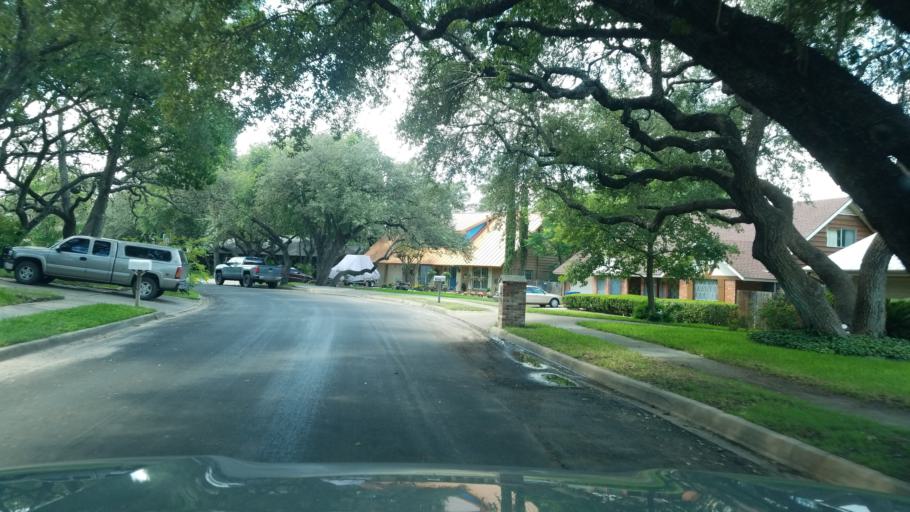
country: US
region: Texas
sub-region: Bexar County
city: Castle Hills
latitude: 29.5462
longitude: -98.5054
